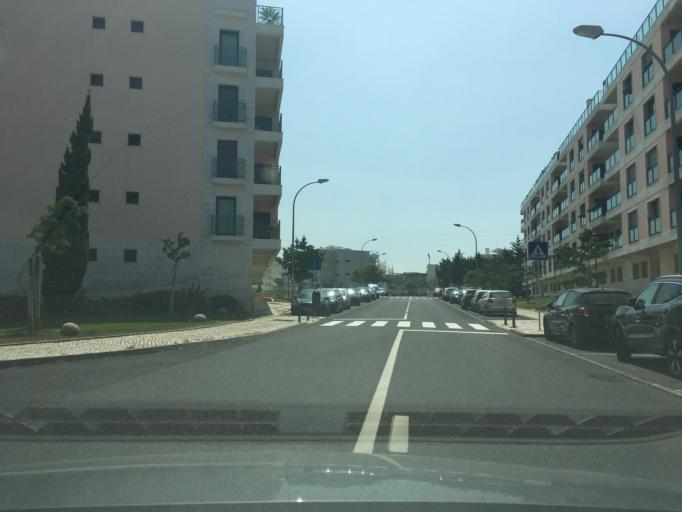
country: PT
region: Lisbon
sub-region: Oeiras
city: Oeiras
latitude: 38.7034
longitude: -9.3097
